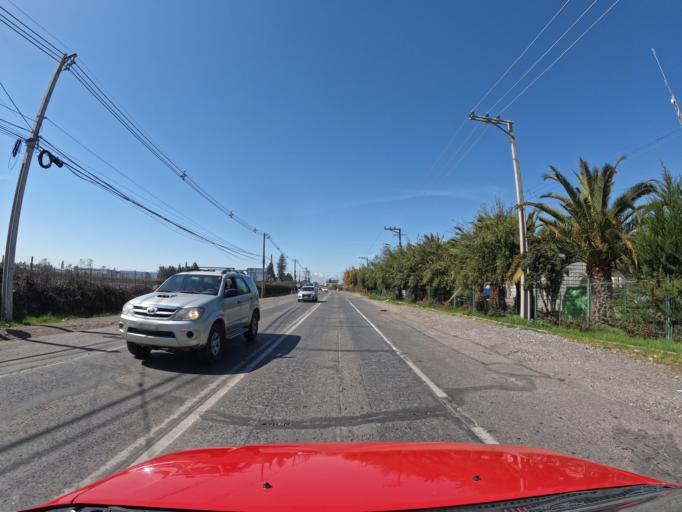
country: CL
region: Maule
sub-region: Provincia de Curico
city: Curico
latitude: -34.9645
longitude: -71.1913
